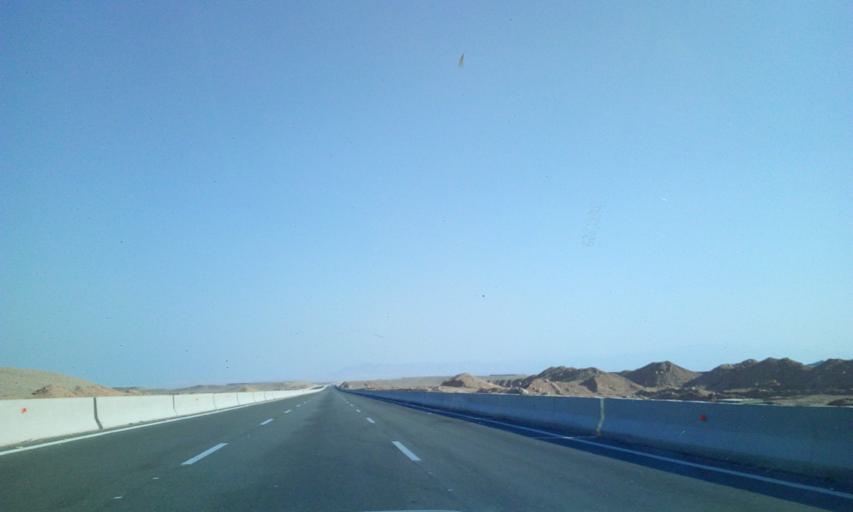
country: EG
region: As Suways
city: Ain Sukhna
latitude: 29.2340
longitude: 32.4851
